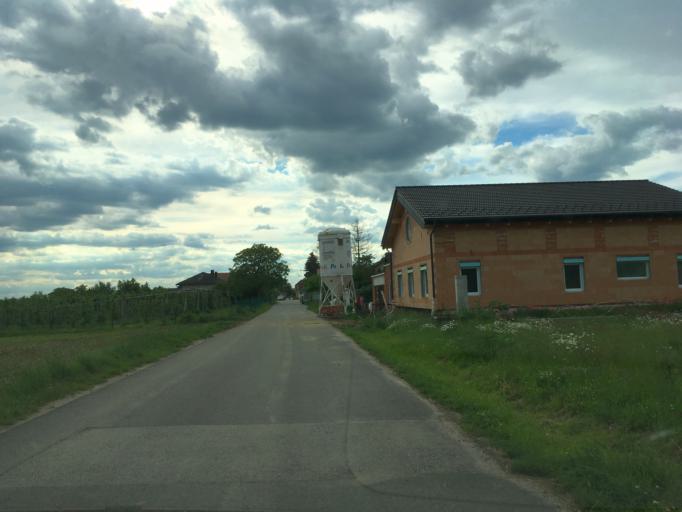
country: AT
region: Lower Austria
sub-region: Politischer Bezirk Tulln
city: Kirchberg am Wagram
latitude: 48.4065
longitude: 15.8992
